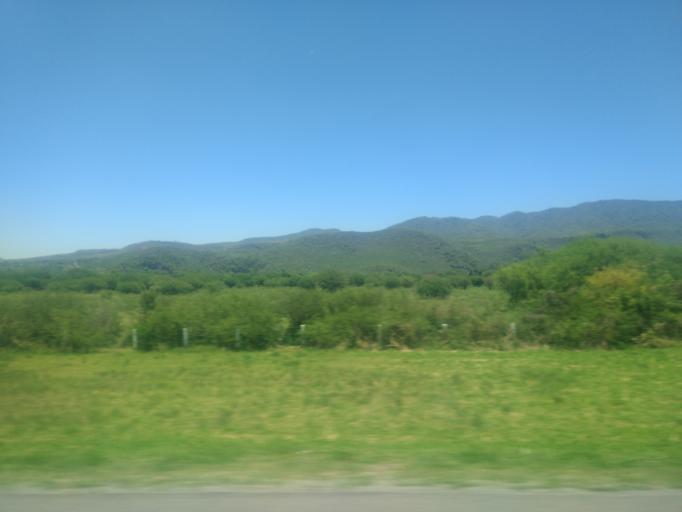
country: MX
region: Jalisco
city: Atoyac
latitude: 19.9589
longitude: -103.5331
